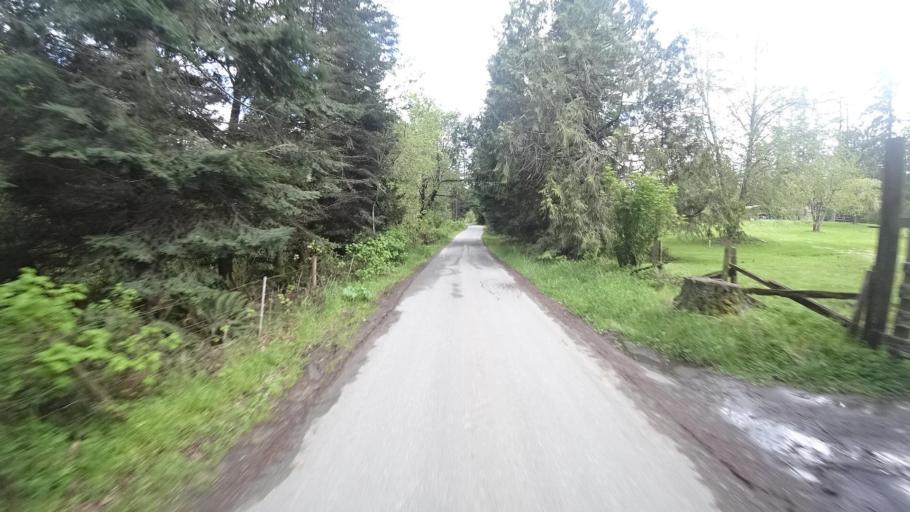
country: US
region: California
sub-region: Humboldt County
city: Blue Lake
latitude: 40.9086
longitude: -123.9720
